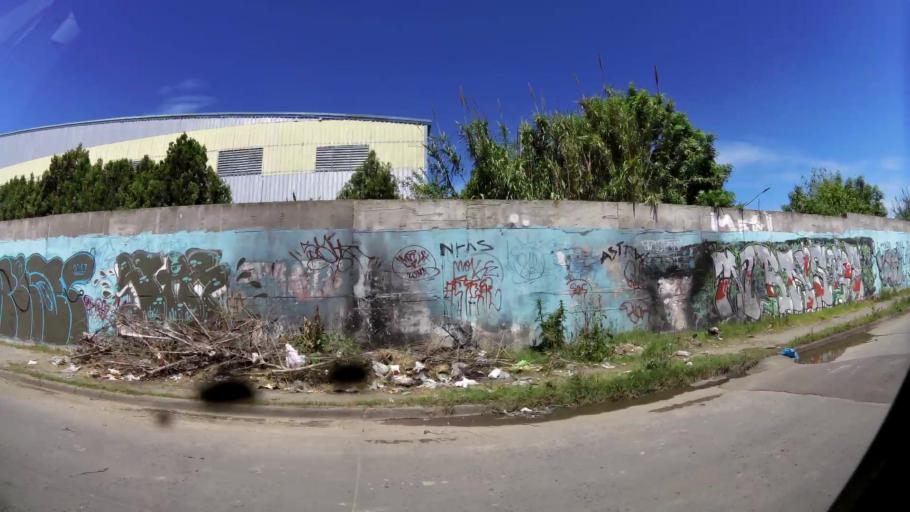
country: AR
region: Buenos Aires
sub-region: Partido de Lanus
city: Lanus
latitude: -34.7353
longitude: -58.3426
